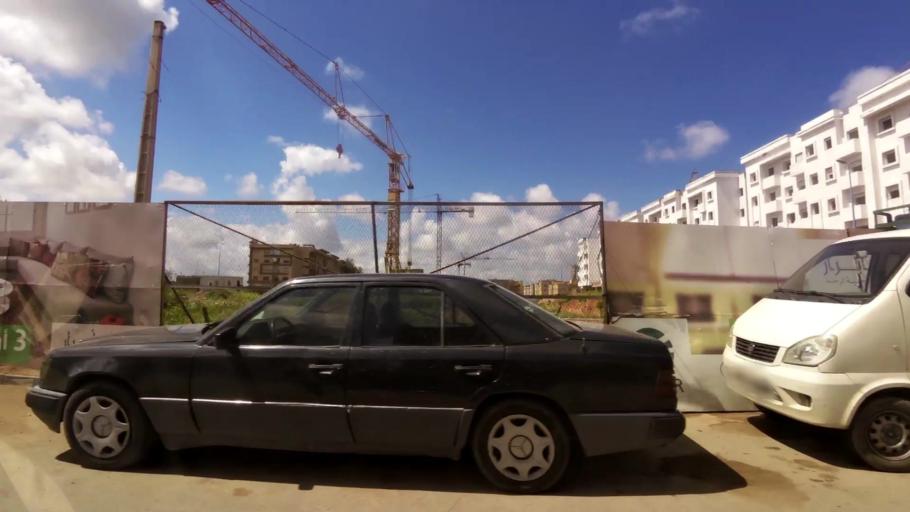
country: MA
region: Grand Casablanca
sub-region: Nouaceur
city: Dar Bouazza
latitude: 33.5319
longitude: -7.7298
